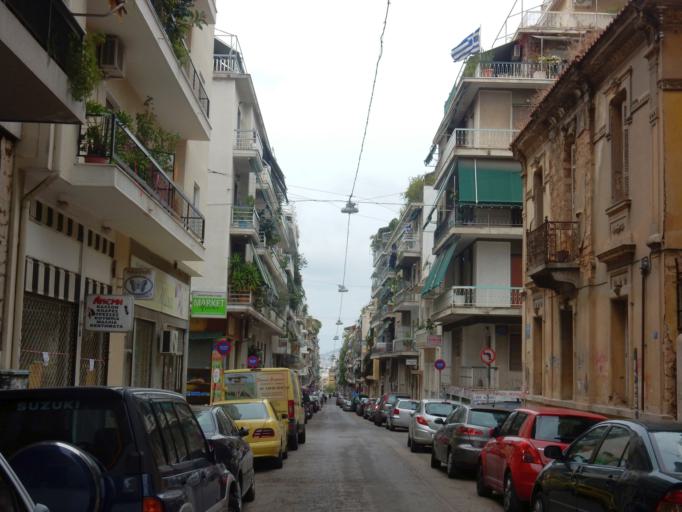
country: GR
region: Attica
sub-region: Nomarchia Athinas
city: Nea Chalkidona
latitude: 38.0154
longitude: 23.7350
